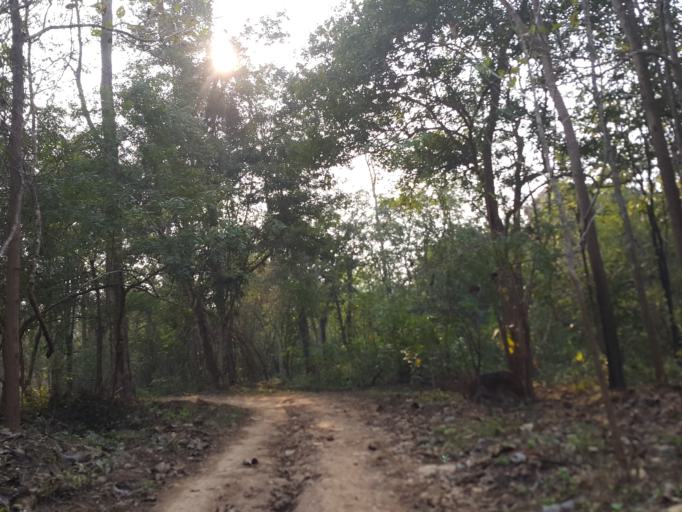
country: TH
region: Lamphun
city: Li
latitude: 17.6104
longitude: 98.9552
